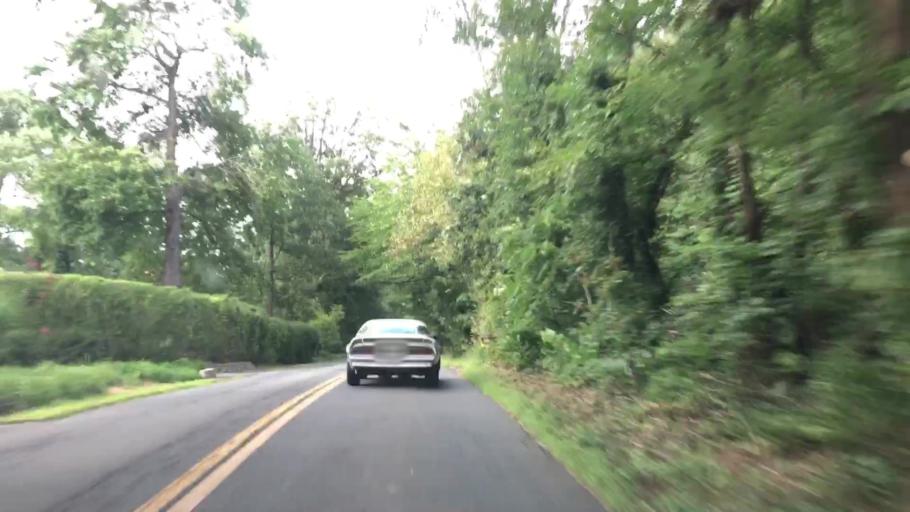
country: US
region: Virginia
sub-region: Prince William County
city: Gainesville
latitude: 38.7445
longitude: -77.6498
